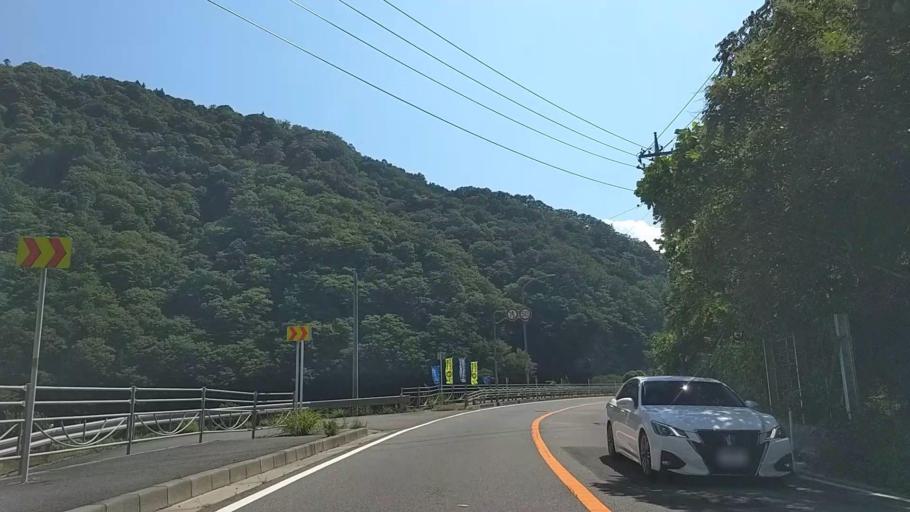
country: JP
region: Yamanashi
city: Ryuo
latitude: 35.5100
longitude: 138.4574
